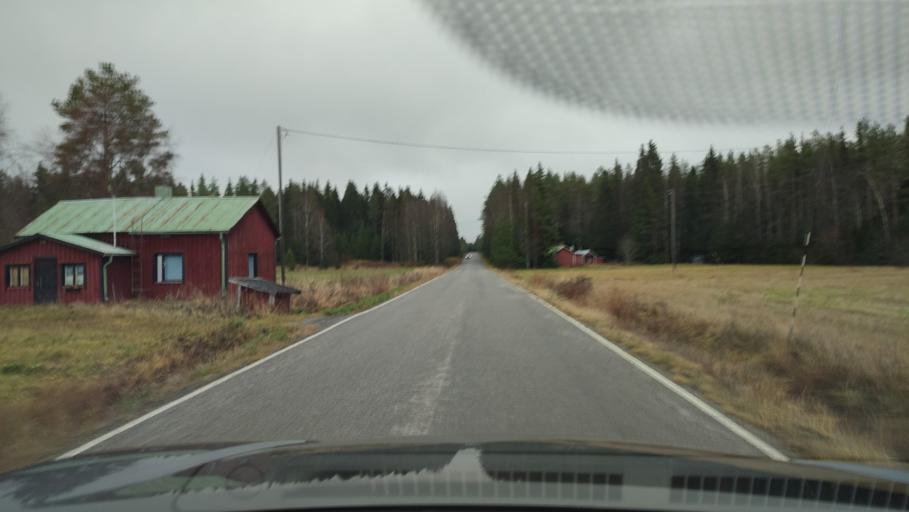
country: FI
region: Southern Ostrobothnia
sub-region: Suupohja
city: Isojoki
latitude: 62.1847
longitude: 21.9338
